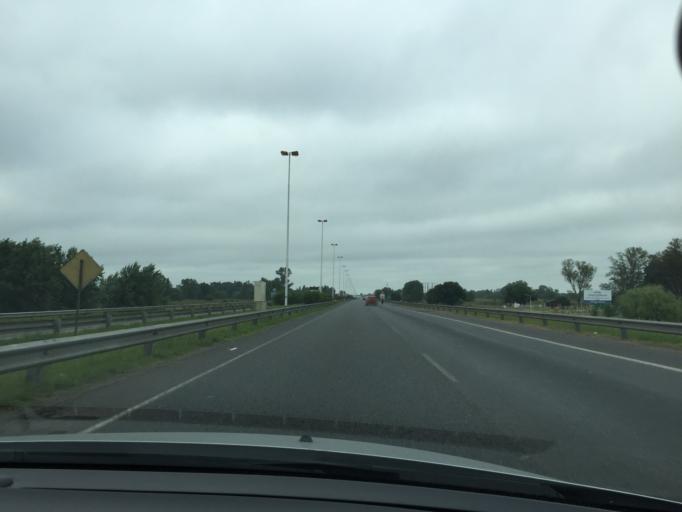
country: AR
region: Buenos Aires
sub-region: Partido de Ezeiza
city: Ezeiza
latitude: -34.8667
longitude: -58.5755
